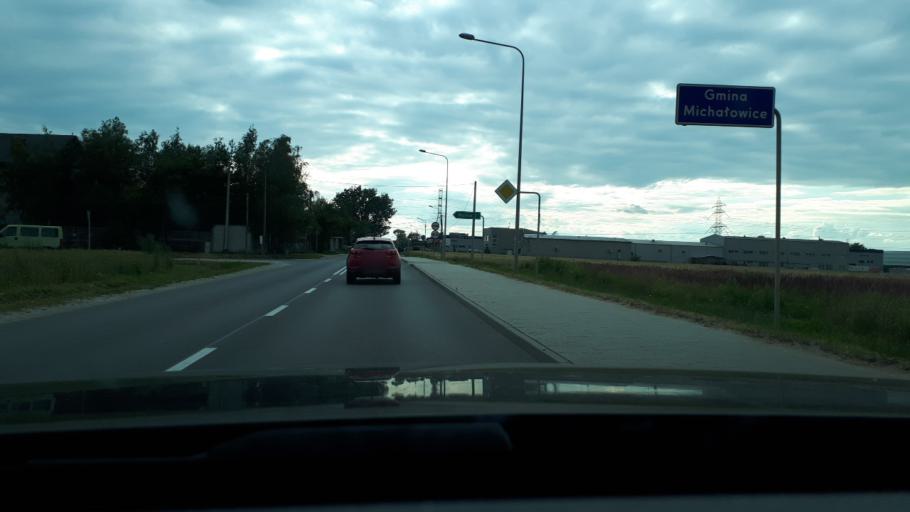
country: PL
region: Masovian Voivodeship
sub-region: Powiat pruszkowski
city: Michalowice
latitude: 52.1437
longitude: 20.8779
